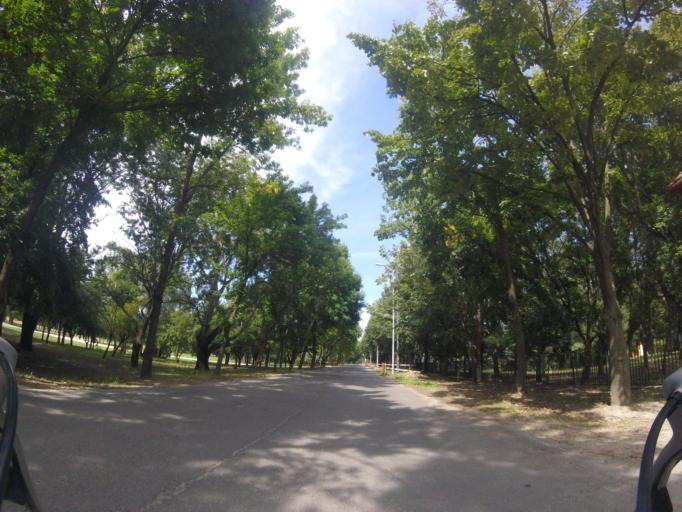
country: HU
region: Budapest
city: Budapest III. keruelet
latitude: 47.5531
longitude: 19.0573
